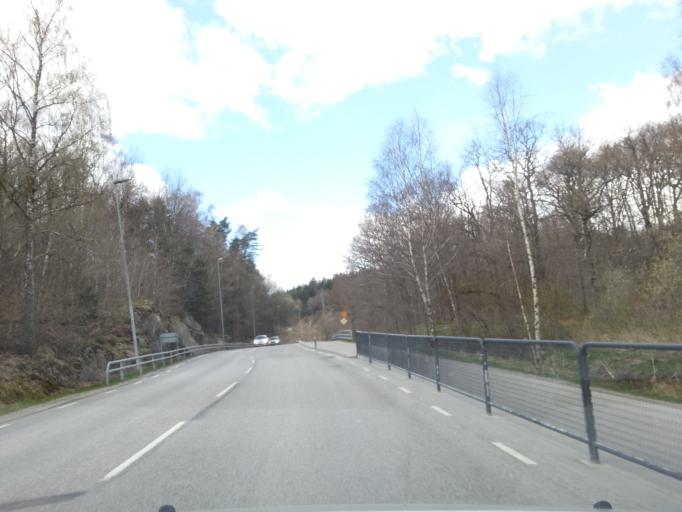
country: SE
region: Vaestra Goetaland
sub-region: Kungalvs Kommun
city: Kungalv
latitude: 57.8881
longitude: 11.9617
